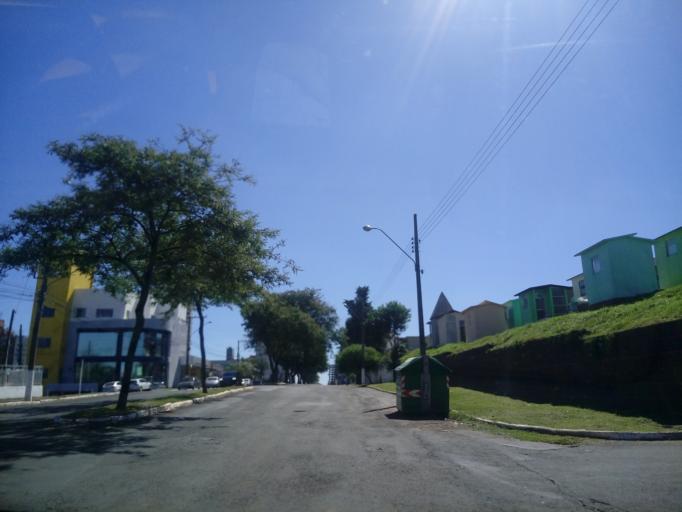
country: BR
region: Santa Catarina
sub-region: Chapeco
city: Chapeco
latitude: -27.1137
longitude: -52.6138
